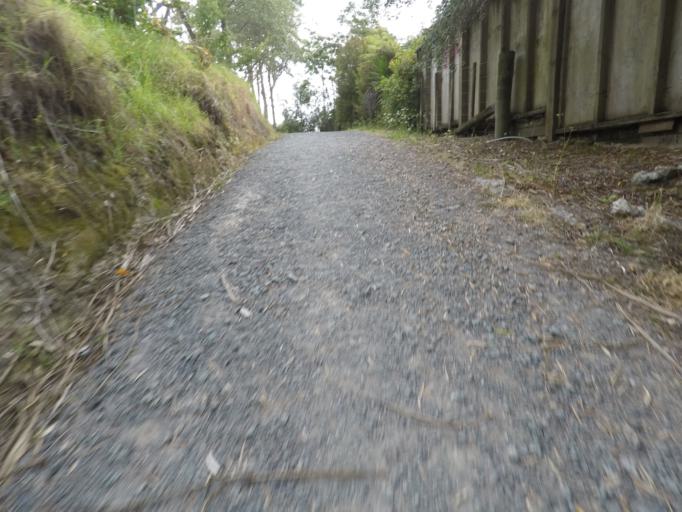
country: NZ
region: Northland
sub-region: Whangarei
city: Whangarei
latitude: -35.7159
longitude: 174.3298
